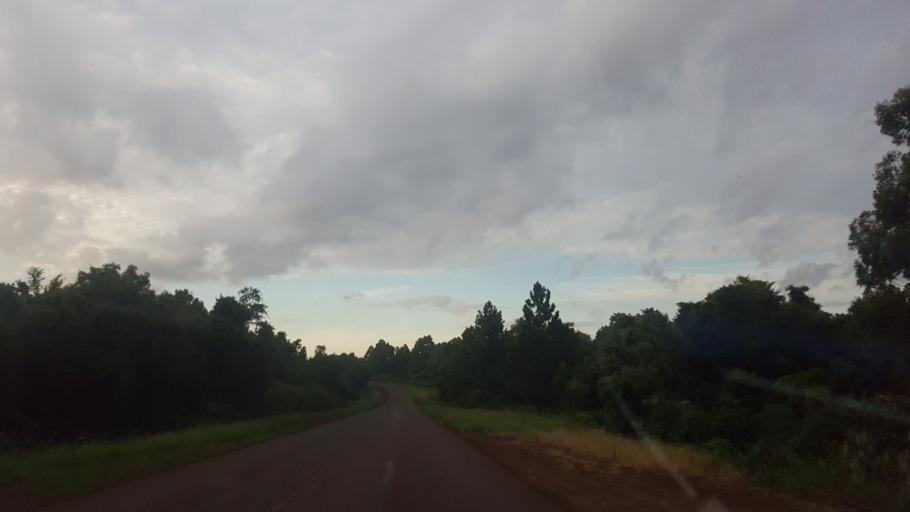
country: AR
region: Misiones
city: Dos de Mayo
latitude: -26.9473
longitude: -54.7146
